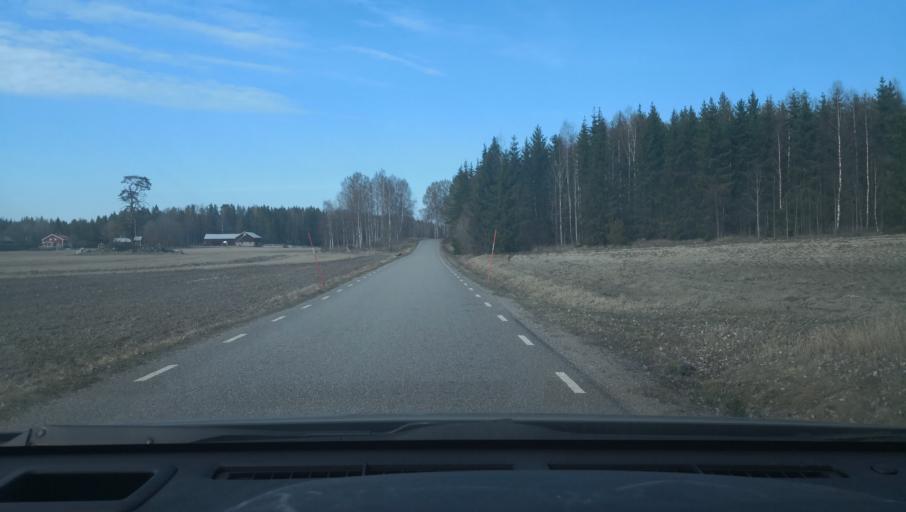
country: SE
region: Uppsala
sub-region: Heby Kommun
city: Heby
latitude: 59.8951
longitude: 16.7992
